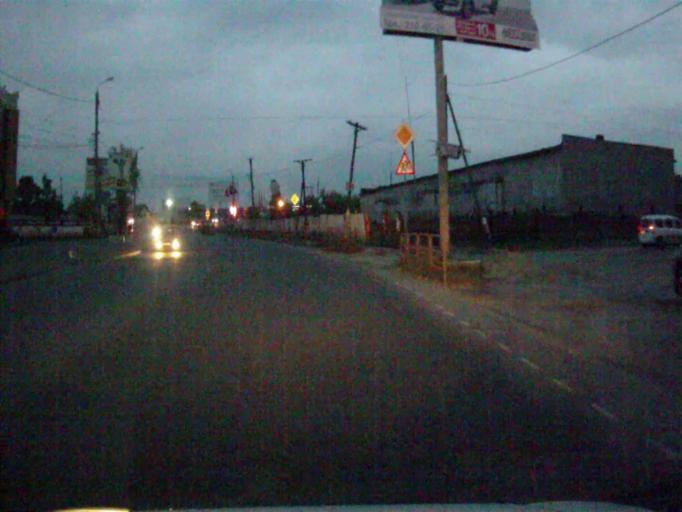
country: RU
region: Chelyabinsk
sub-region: Gorod Chelyabinsk
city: Chelyabinsk
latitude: 55.1539
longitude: 61.3027
